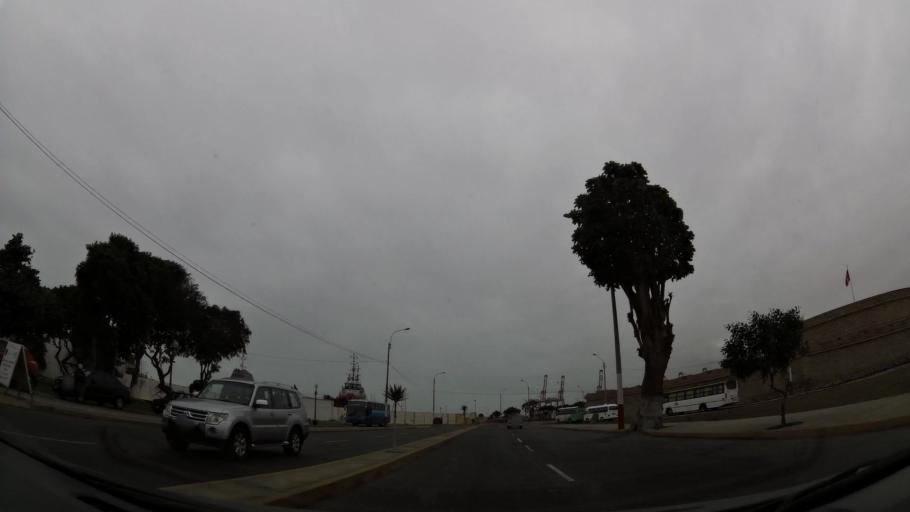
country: PE
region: Callao
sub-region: Callao
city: Callao
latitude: -12.0632
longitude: -77.1511
